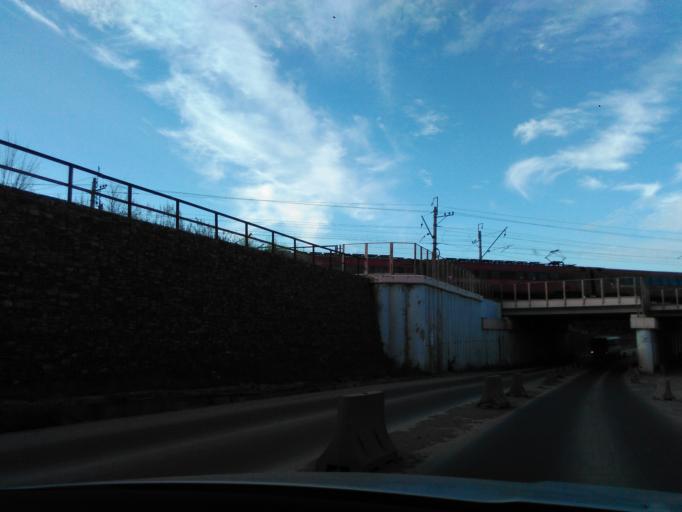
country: RU
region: Moskovskaya
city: Sheremet'yevskiy
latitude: 55.9757
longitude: 37.4541
